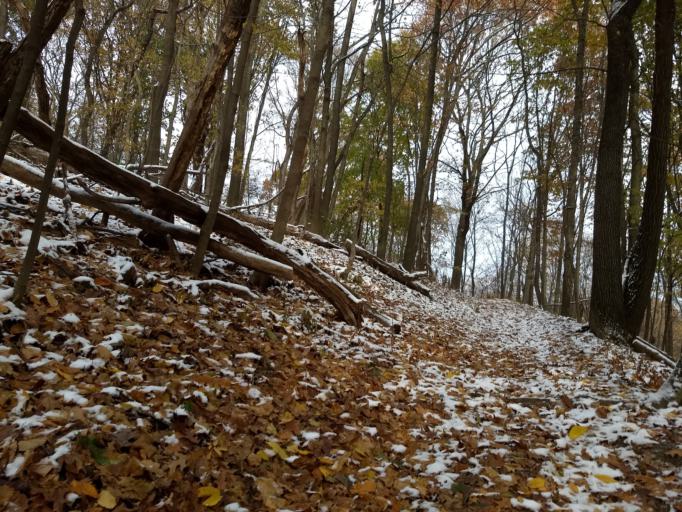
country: US
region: Pennsylvania
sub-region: Allegheny County
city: Mount Oliver
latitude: 40.4056
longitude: -80.0080
